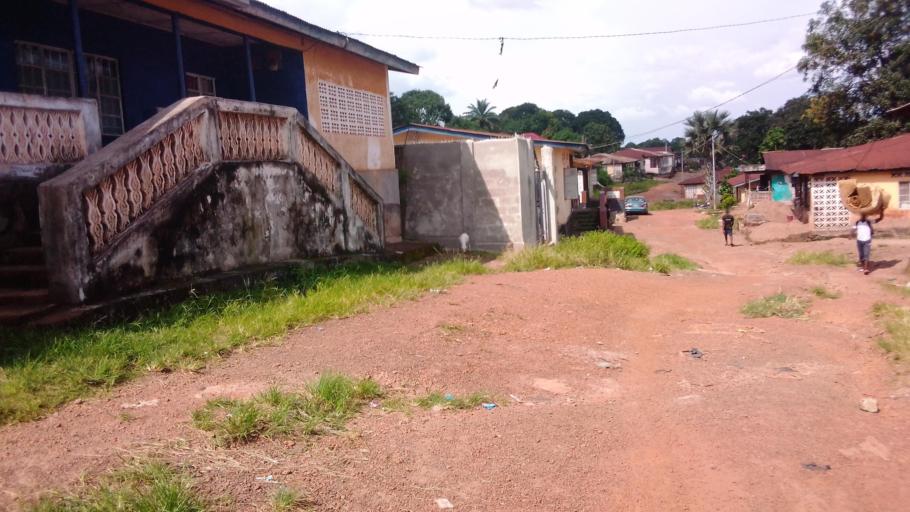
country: SL
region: Northern Province
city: Makeni
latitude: 8.8893
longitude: -12.0365
